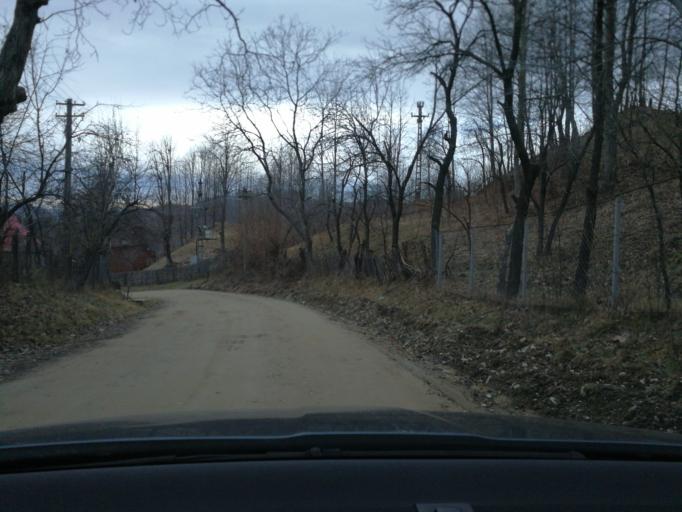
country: RO
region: Dambovita
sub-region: Comuna Bezdead
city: Bezdead
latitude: 45.1696
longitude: 25.5463
